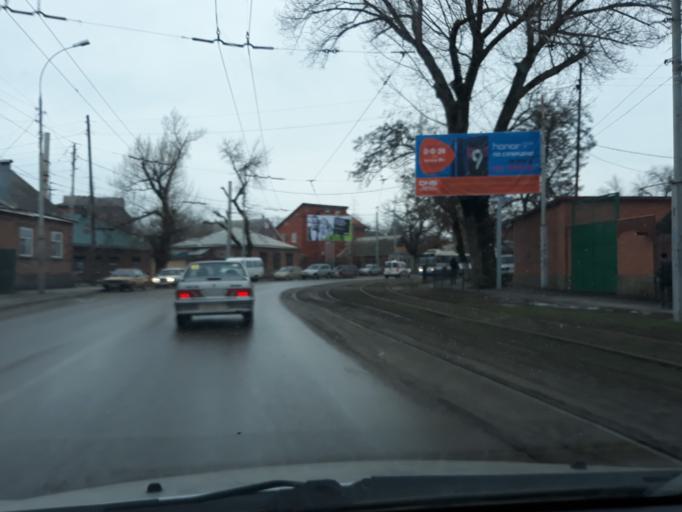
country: RU
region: Rostov
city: Taganrog
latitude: 47.2249
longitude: 38.9179
